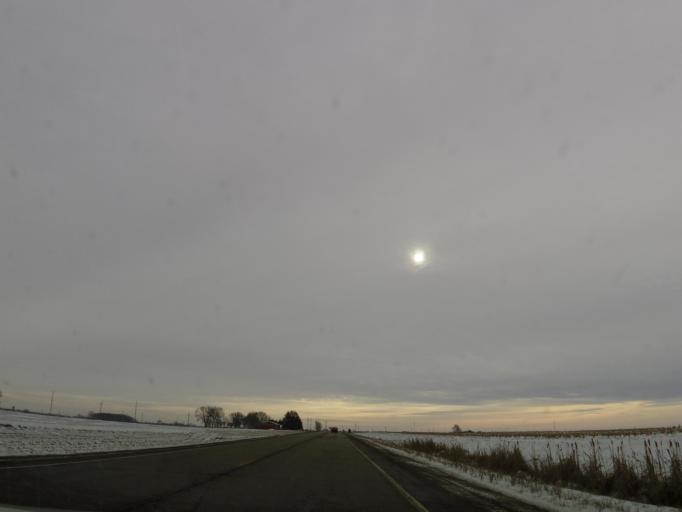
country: US
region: Illinois
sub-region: LaSalle County
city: Oglesby
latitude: 41.2864
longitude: -89.0922
